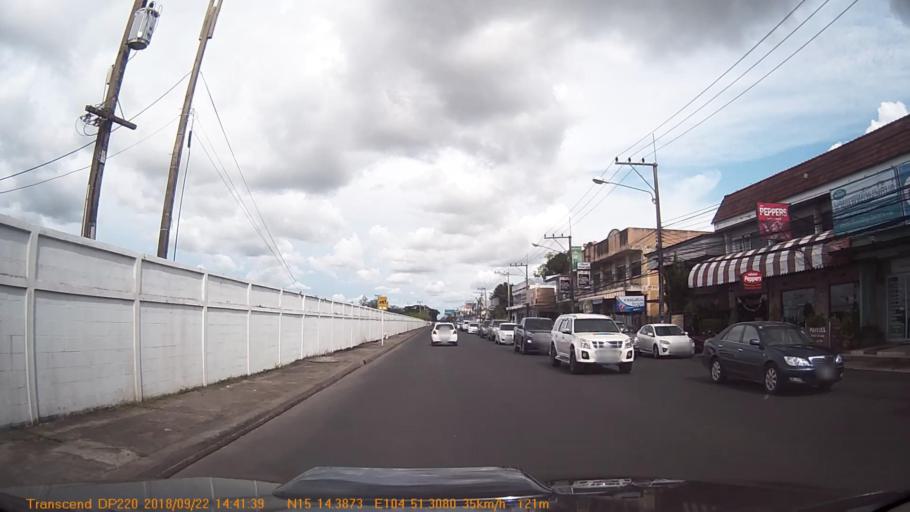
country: TH
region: Changwat Ubon Ratchathani
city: Ubon Ratchathani
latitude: 15.2398
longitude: 104.8555
